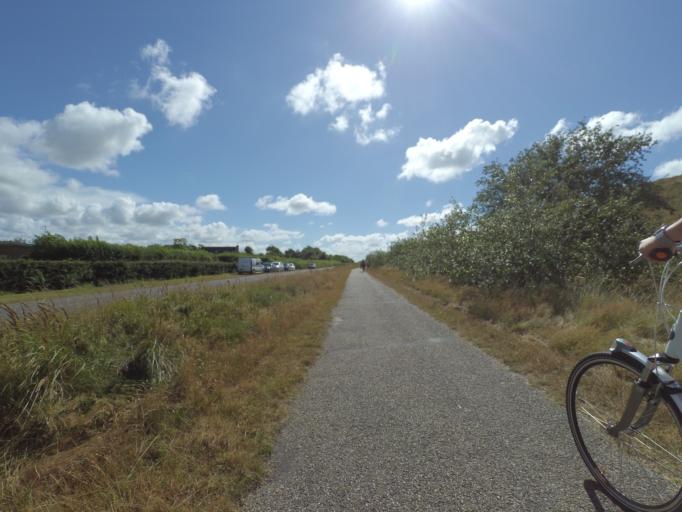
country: NL
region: North Holland
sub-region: Gemeente Texel
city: Den Burg
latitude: 53.1276
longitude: 4.8128
